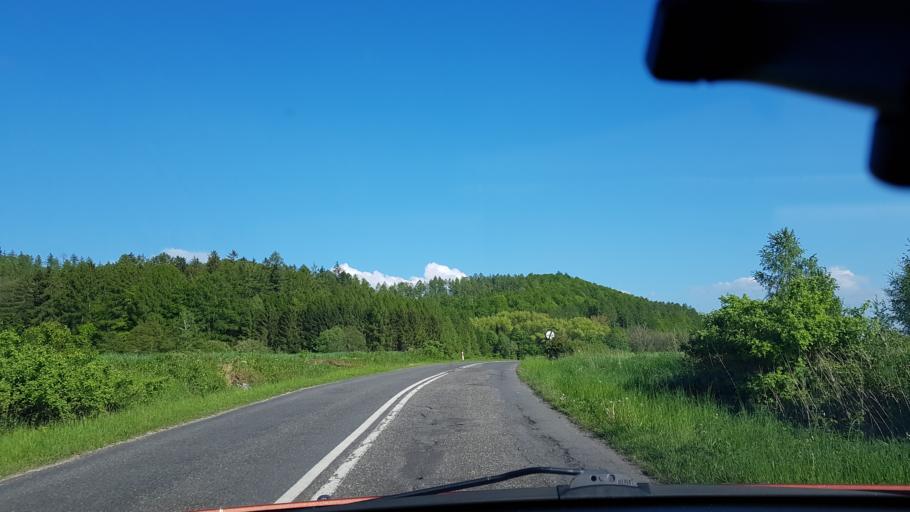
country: PL
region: Lower Silesian Voivodeship
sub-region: Powiat klodzki
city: Bozkow
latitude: 50.5871
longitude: 16.5812
